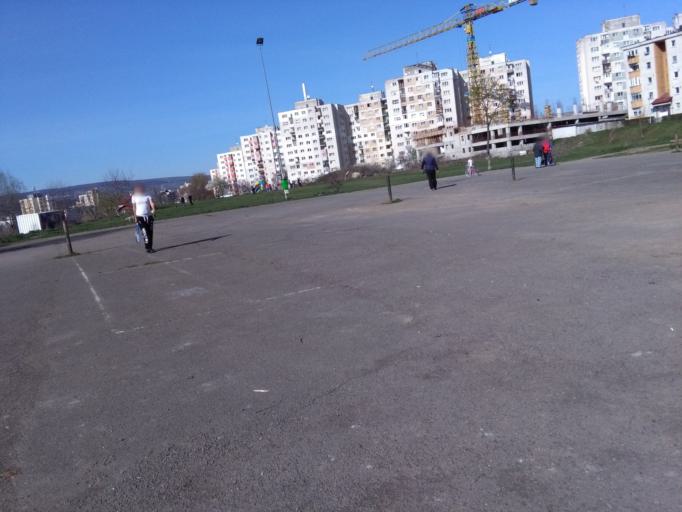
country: RO
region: Cluj
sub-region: Municipiul Cluj-Napoca
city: Cluj-Napoca
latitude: 46.7491
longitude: 23.5547
